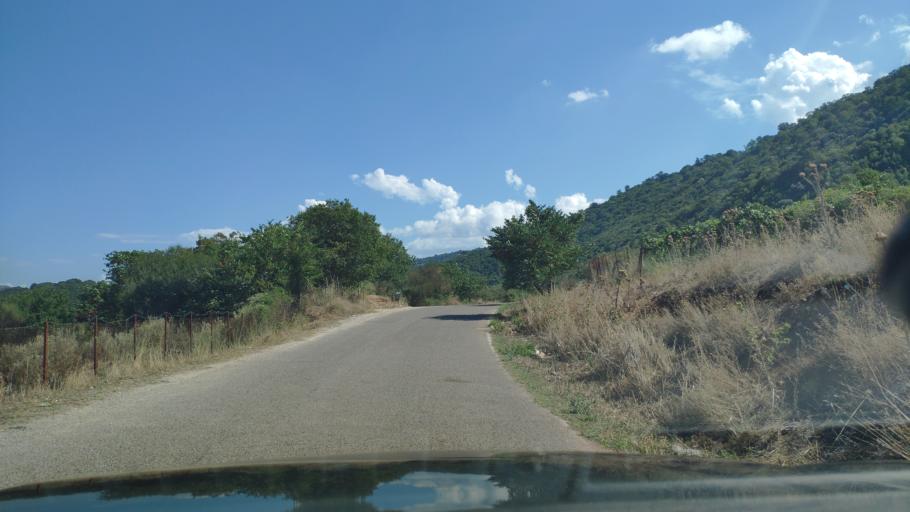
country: GR
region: West Greece
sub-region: Nomos Aitolias kai Akarnanias
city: Katouna
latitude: 38.8322
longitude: 21.0993
